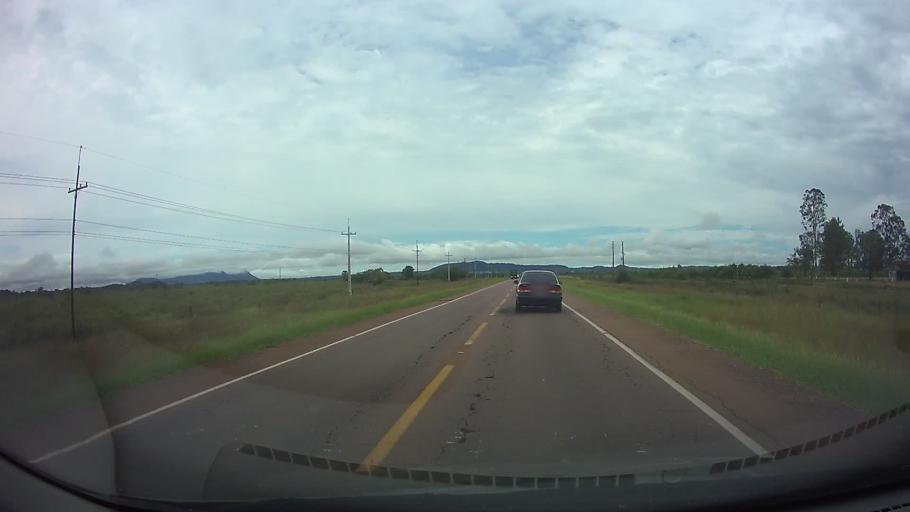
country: PY
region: Paraguari
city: Carapegua
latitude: -25.7318
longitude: -57.2076
